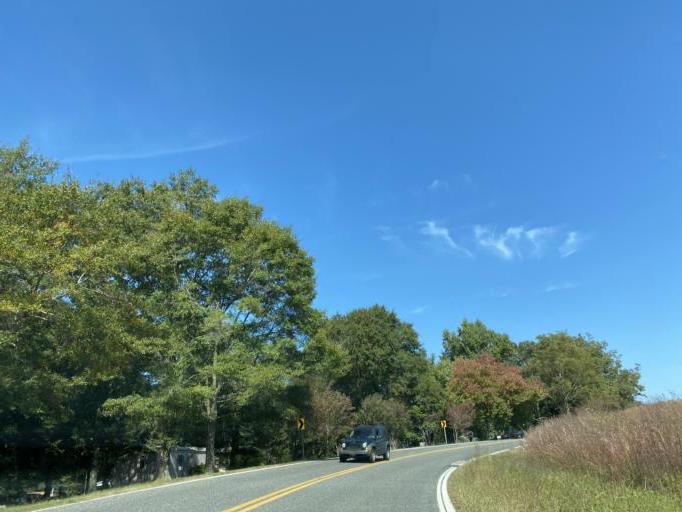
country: US
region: North Carolina
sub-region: Cleveland County
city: Boiling Springs
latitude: 35.2914
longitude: -81.6704
